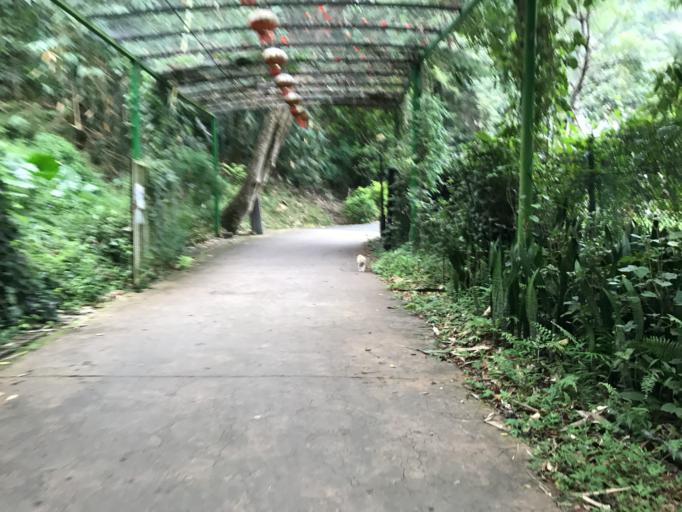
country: TW
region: Taiwan
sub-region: Nantou
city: Puli
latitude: 23.9623
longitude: 120.9968
